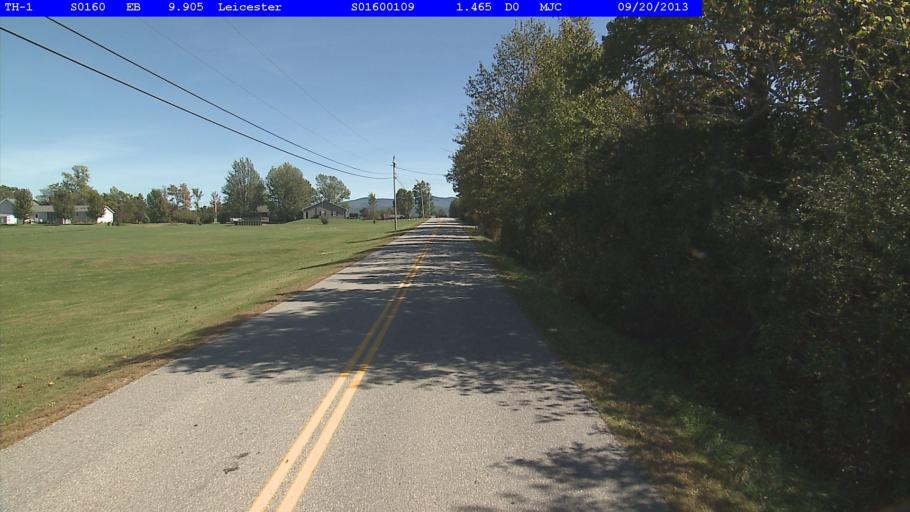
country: US
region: Vermont
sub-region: Rutland County
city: Brandon
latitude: 43.8562
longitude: -73.1308
